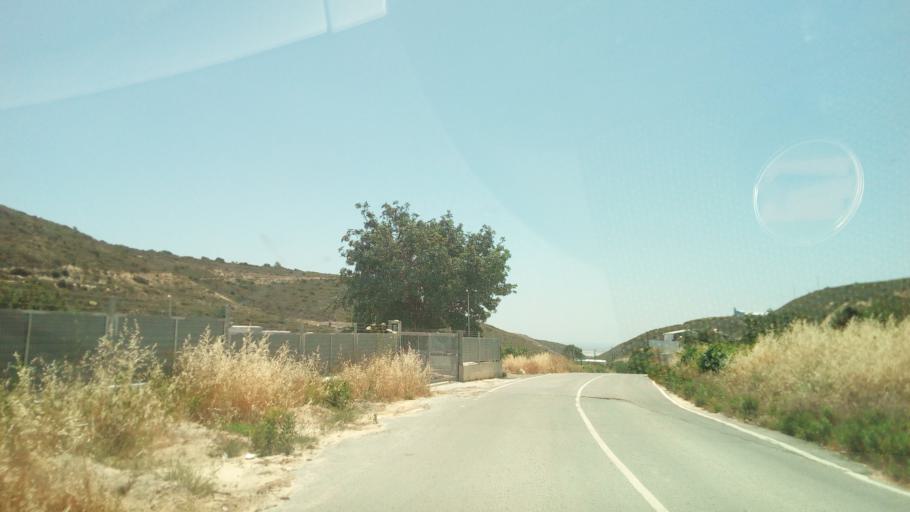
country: CY
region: Limassol
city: Ypsonas
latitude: 34.7479
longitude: 32.9429
